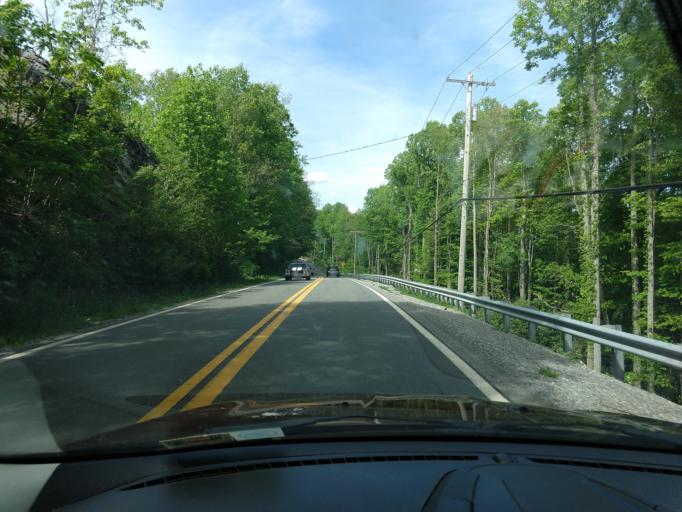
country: US
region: West Virginia
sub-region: Raleigh County
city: Daniels
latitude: 37.7807
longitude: -81.1144
